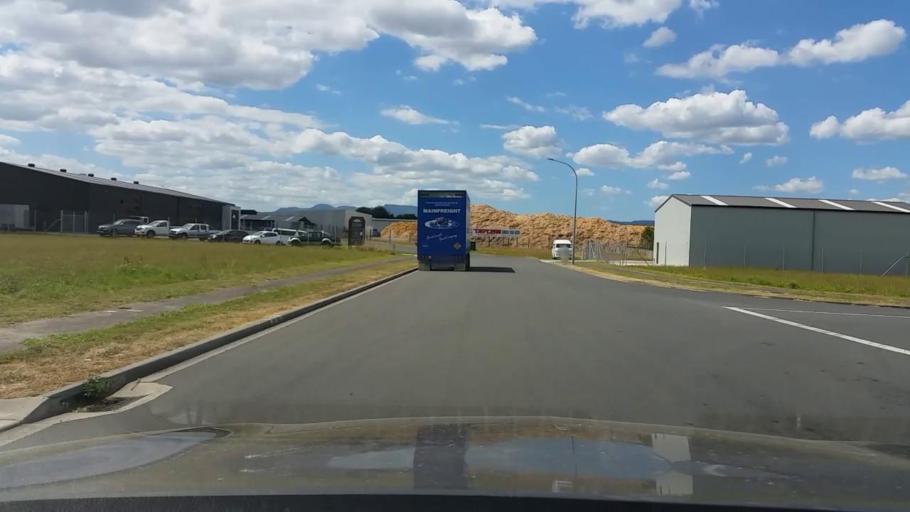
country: NZ
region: Waikato
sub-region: Matamata-Piako District
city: Matamata
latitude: -37.8184
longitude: 175.7960
